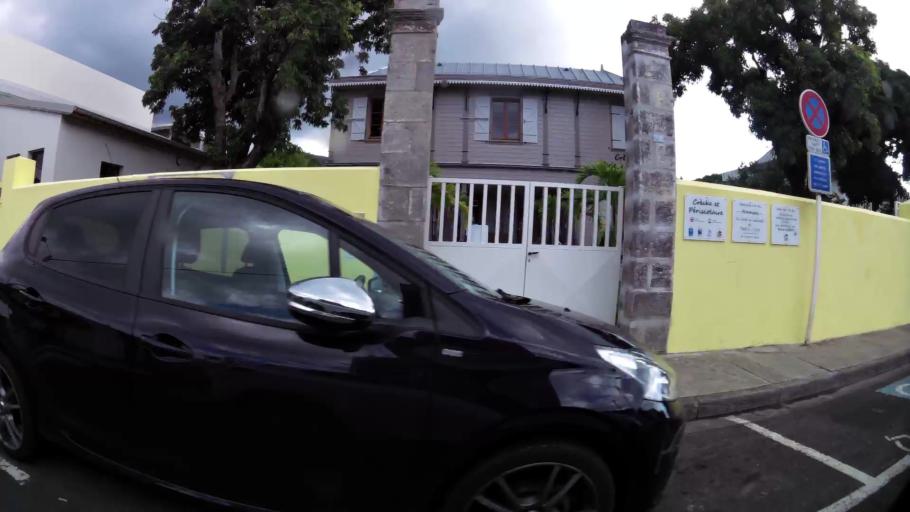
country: RE
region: Reunion
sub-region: Reunion
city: Saint-Denis
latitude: -20.8834
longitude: 55.4545
